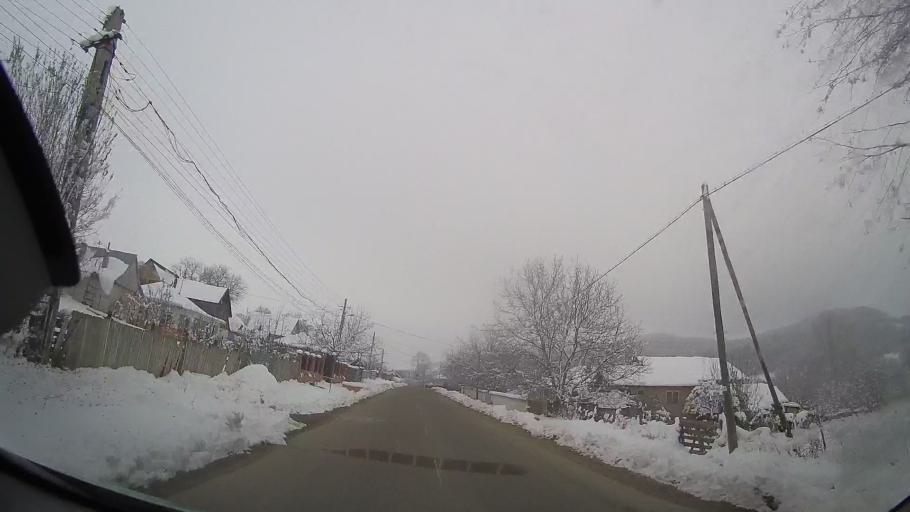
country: RO
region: Neamt
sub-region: Comuna Bozieni
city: Bozieni
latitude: 46.8354
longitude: 27.1587
